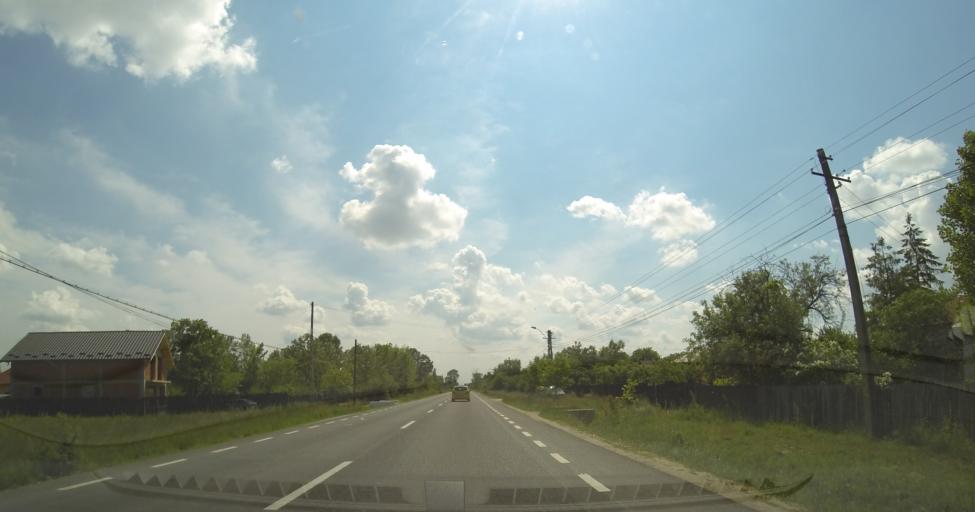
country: RO
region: Arges
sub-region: Comuna Lunca Corbului
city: Lunca Corbului
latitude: 44.6949
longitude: 24.7736
